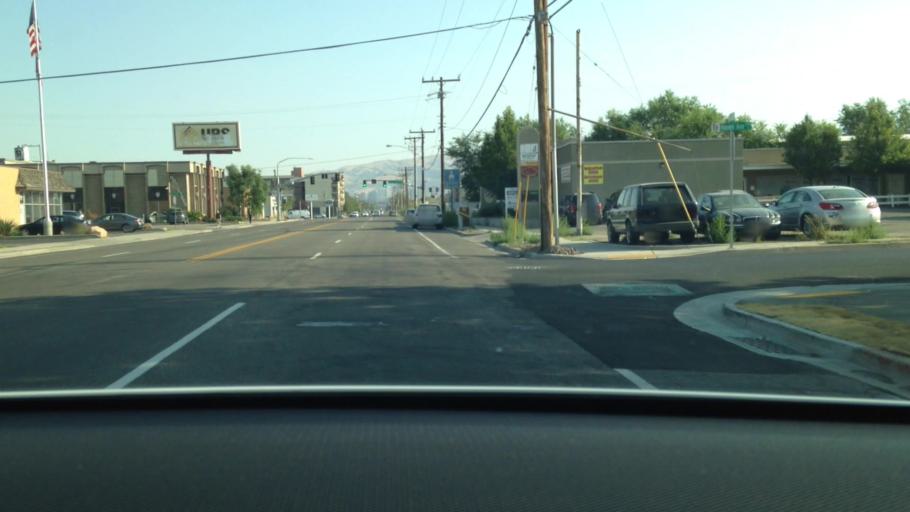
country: US
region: Utah
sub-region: Salt Lake County
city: South Salt Lake
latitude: 40.7208
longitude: -111.8911
